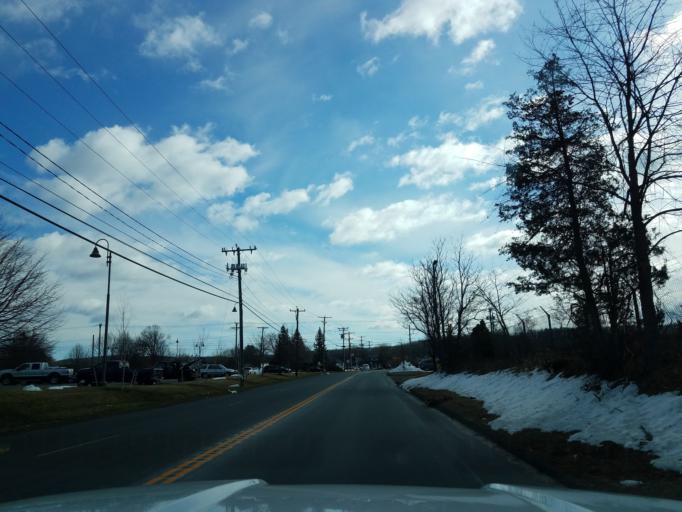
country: US
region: Connecticut
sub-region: Hartford County
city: Plainville
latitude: 41.6408
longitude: -72.8773
